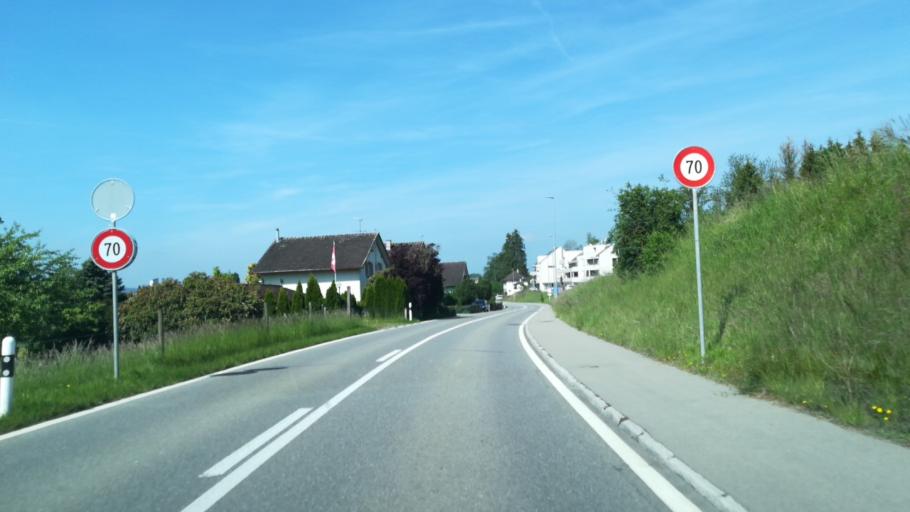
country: CH
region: Thurgau
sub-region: Frauenfeld District
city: Mullheim
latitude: 47.6060
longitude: 9.0164
